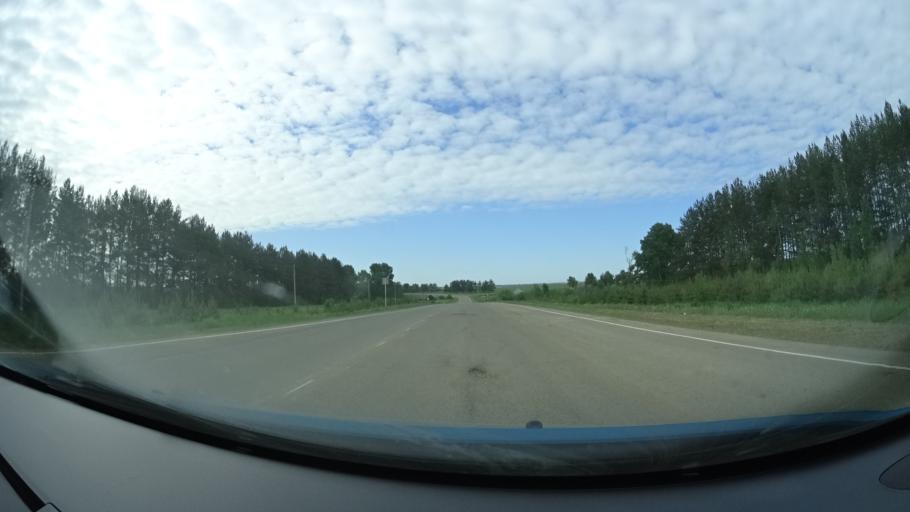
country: RU
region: Perm
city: Kuyeda
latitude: 56.4748
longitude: 55.5895
